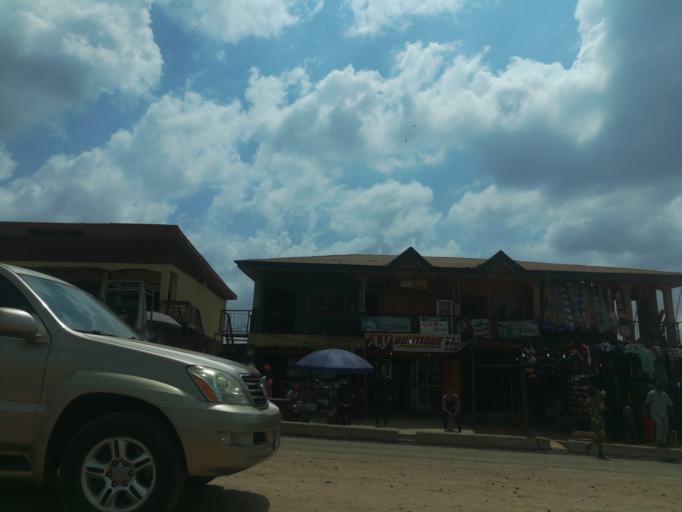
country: NG
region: Oyo
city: Ibadan
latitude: 7.3949
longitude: 3.9183
